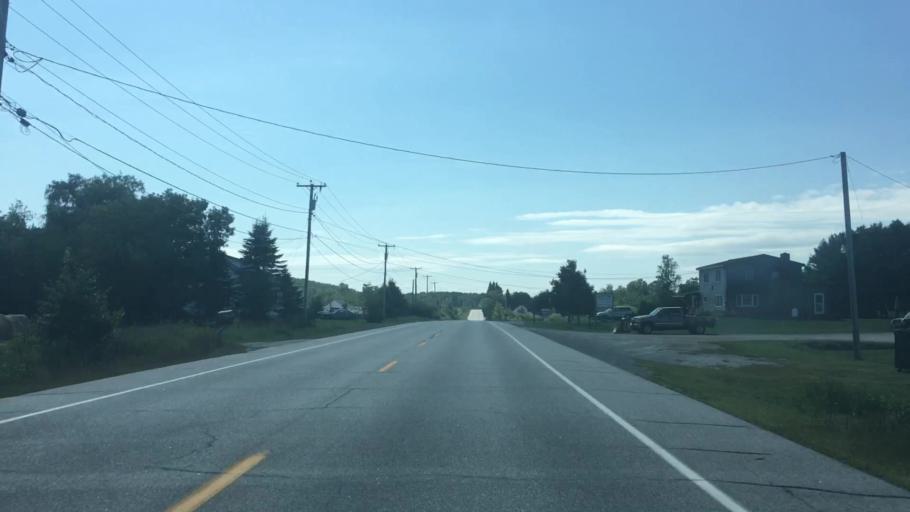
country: US
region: Maine
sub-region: Kennebec County
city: Monmouth
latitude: 44.1782
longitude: -69.9976
